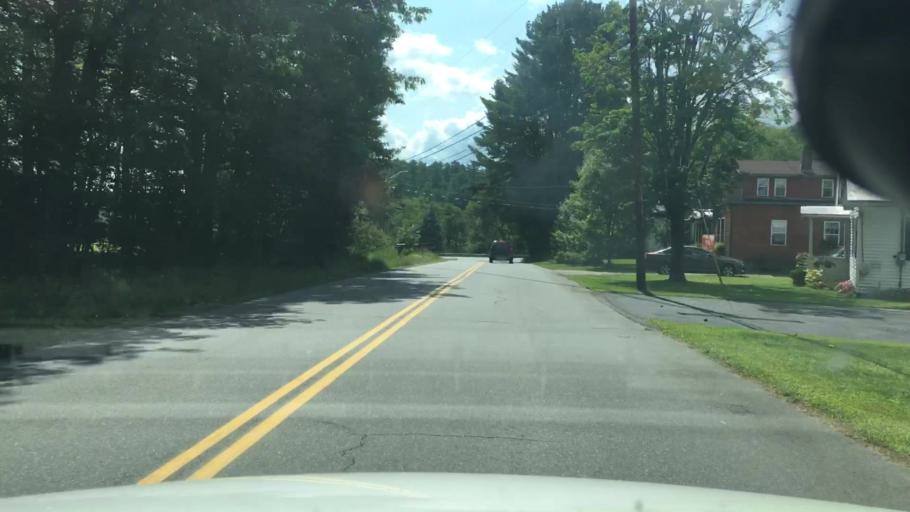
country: US
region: Maine
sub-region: Somerset County
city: Skowhegan
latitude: 44.7743
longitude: -69.7077
